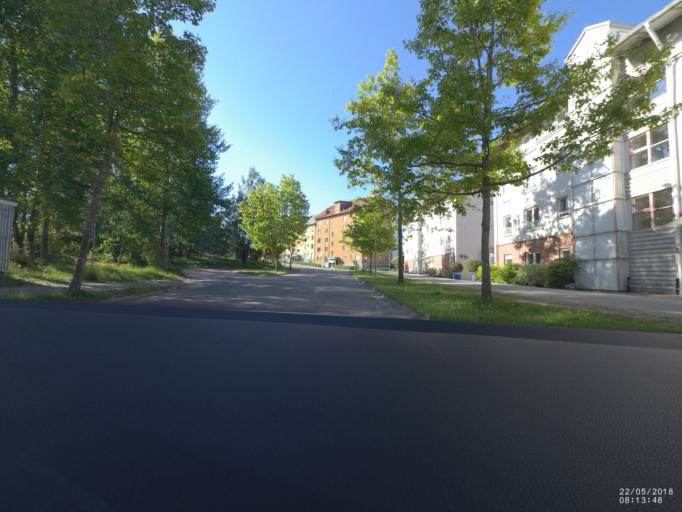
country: SE
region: Soedermanland
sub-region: Nykopings Kommun
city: Nykoping
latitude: 58.7445
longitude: 17.0436
